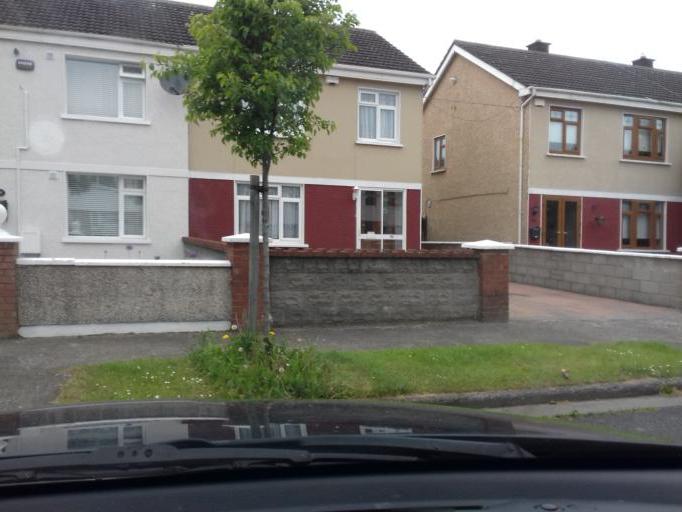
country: IE
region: Leinster
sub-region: Dublin City
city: Finglas
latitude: 53.3990
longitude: -6.3115
